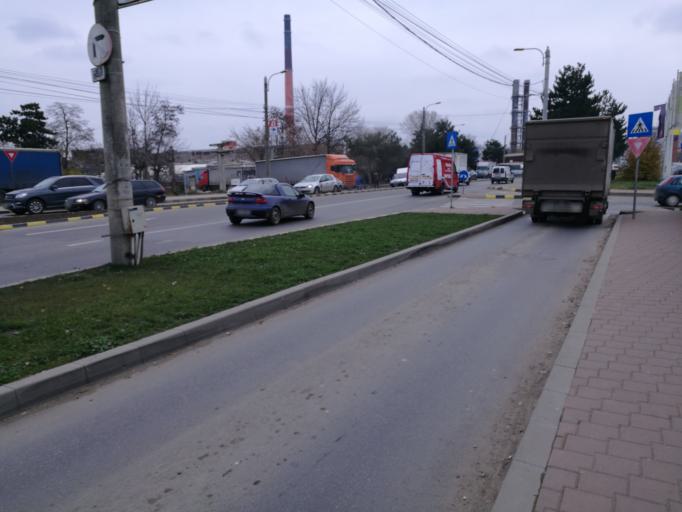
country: RO
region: Suceava
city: Suceava
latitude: 47.6652
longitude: 26.2697
